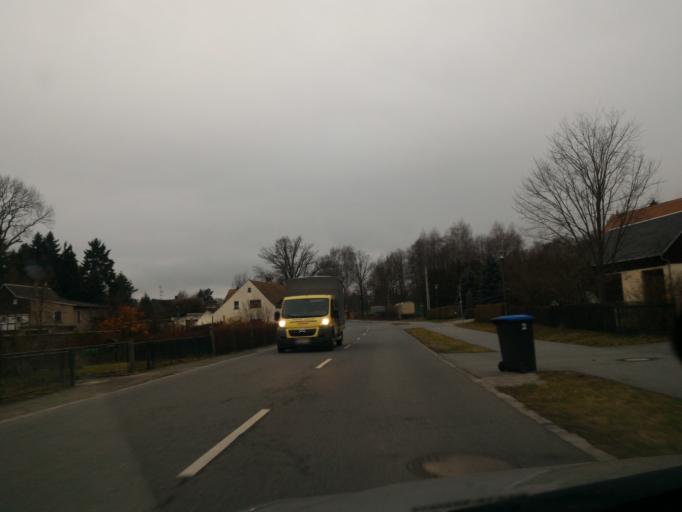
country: DE
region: Saxony
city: Leutersdorf
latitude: 50.9432
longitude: 14.6280
